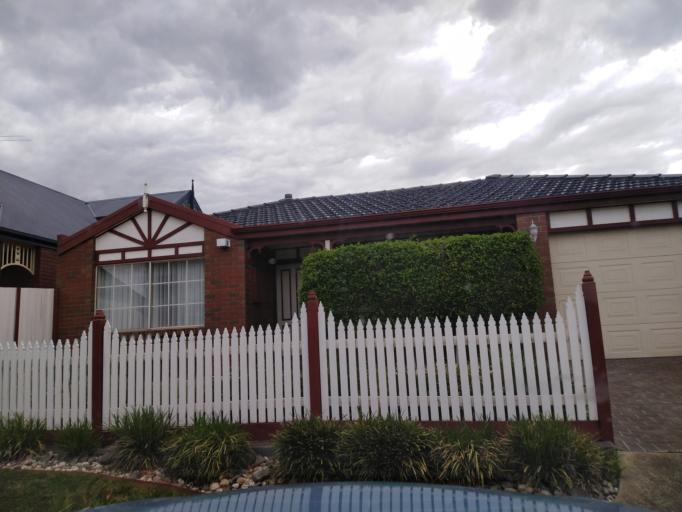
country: AU
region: Victoria
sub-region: Hobsons Bay
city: Williamstown North
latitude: -37.8538
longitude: 144.8720
